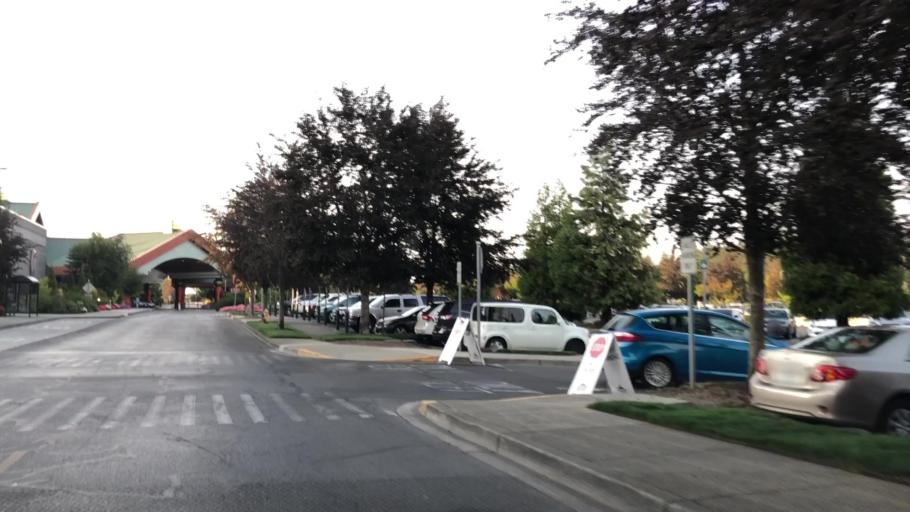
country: US
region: Washington
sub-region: Snohomish County
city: Marysville
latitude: 48.0866
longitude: -122.1887
